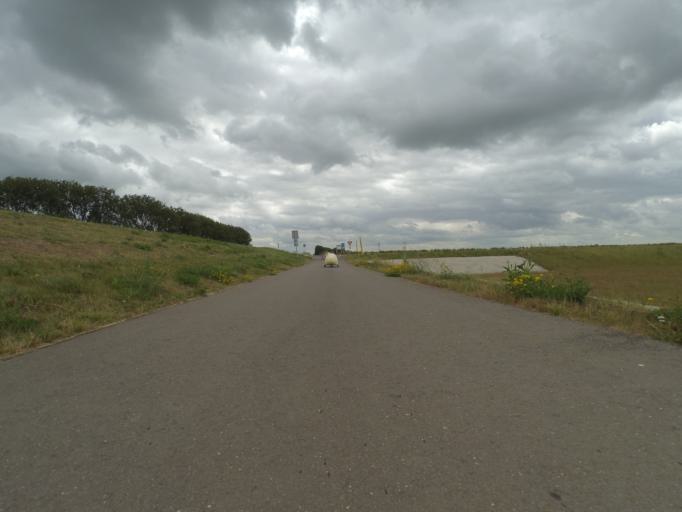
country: NL
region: South Holland
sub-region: Gemeente Hardinxveld-Giessendam
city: Boven-Hardinxveld
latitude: 51.8003
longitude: 4.8651
